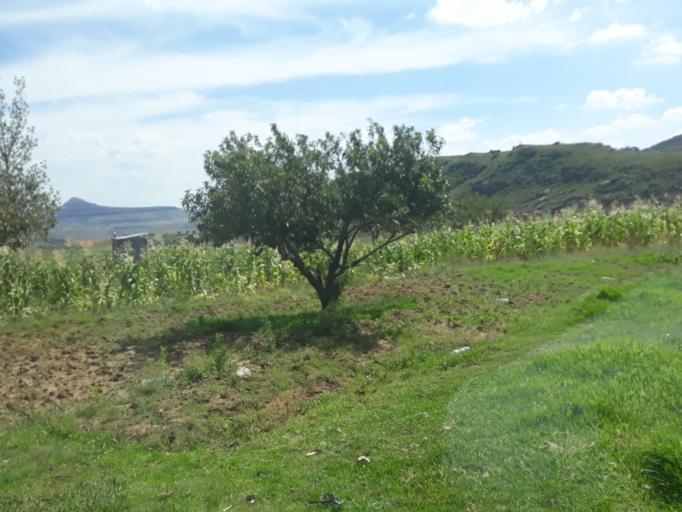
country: LS
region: Mohale's Hoek District
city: Mohale's Hoek
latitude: -30.1004
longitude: 27.4712
